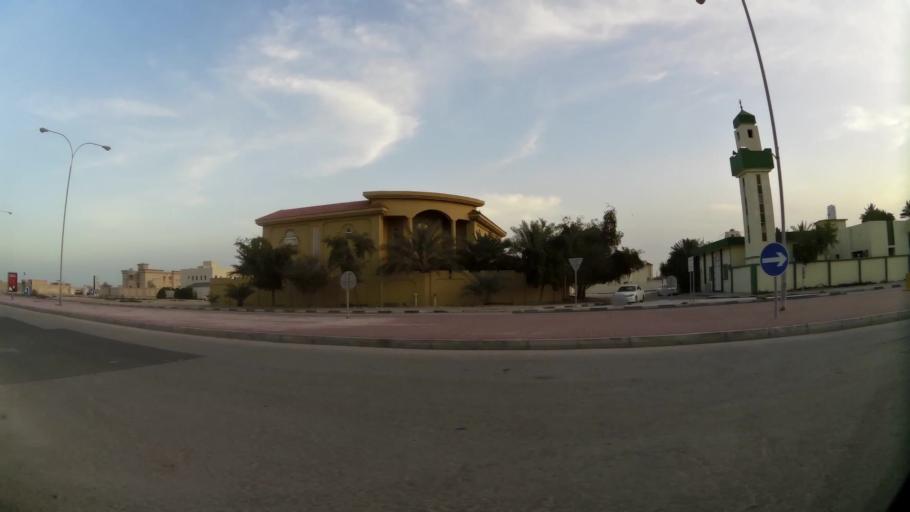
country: QA
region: Al Wakrah
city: Al Wakrah
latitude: 25.1780
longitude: 51.6101
